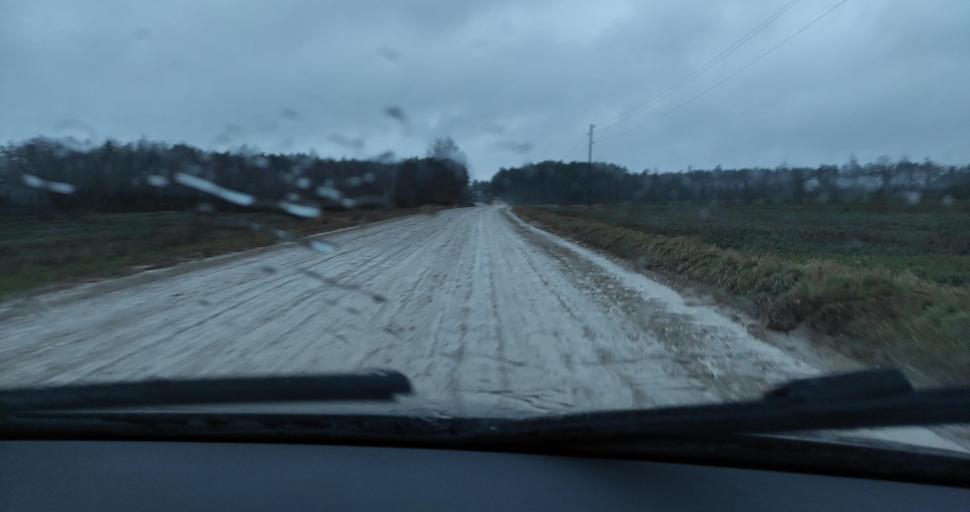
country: LV
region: Skrunda
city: Skrunda
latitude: 56.6819
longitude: 22.2211
